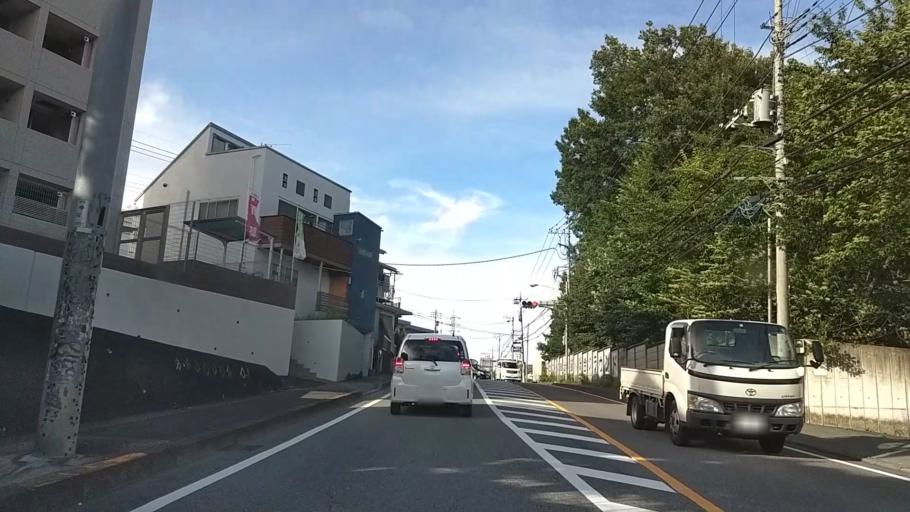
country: JP
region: Tokyo
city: Hachioji
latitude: 35.6409
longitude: 139.3185
